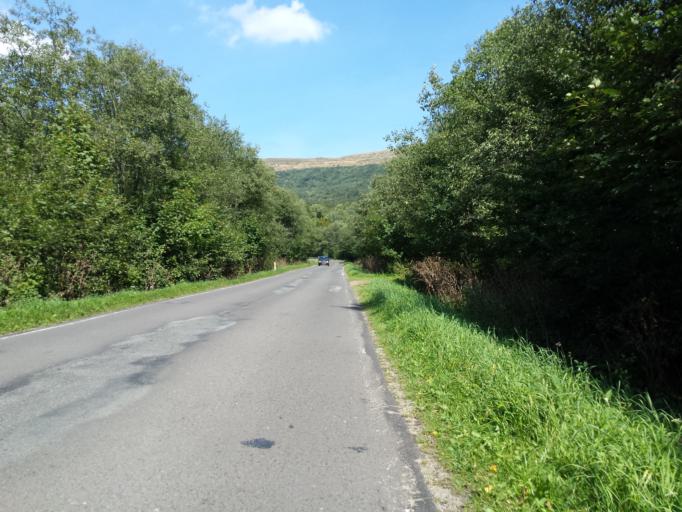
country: PL
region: Subcarpathian Voivodeship
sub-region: Powiat bieszczadzki
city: Lutowiska
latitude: 49.1165
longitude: 22.6100
